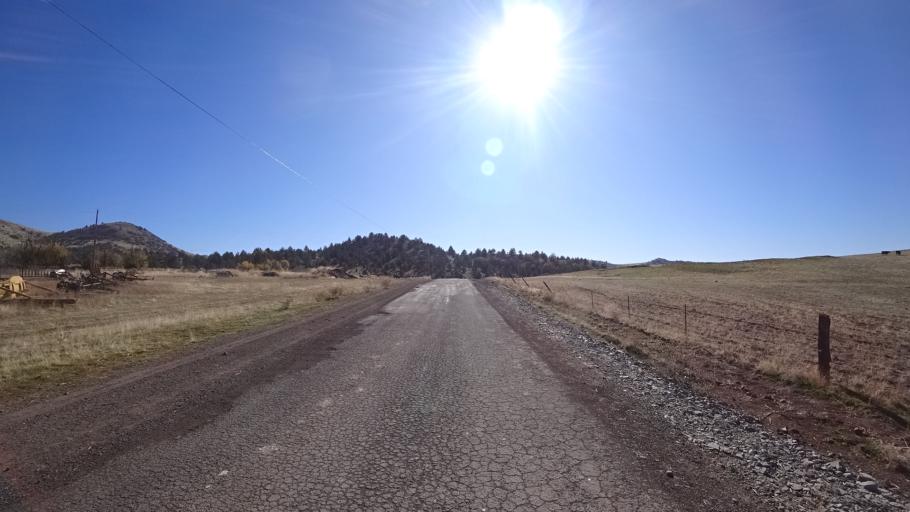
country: US
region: California
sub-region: Siskiyou County
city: Montague
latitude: 41.8110
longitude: -122.3767
